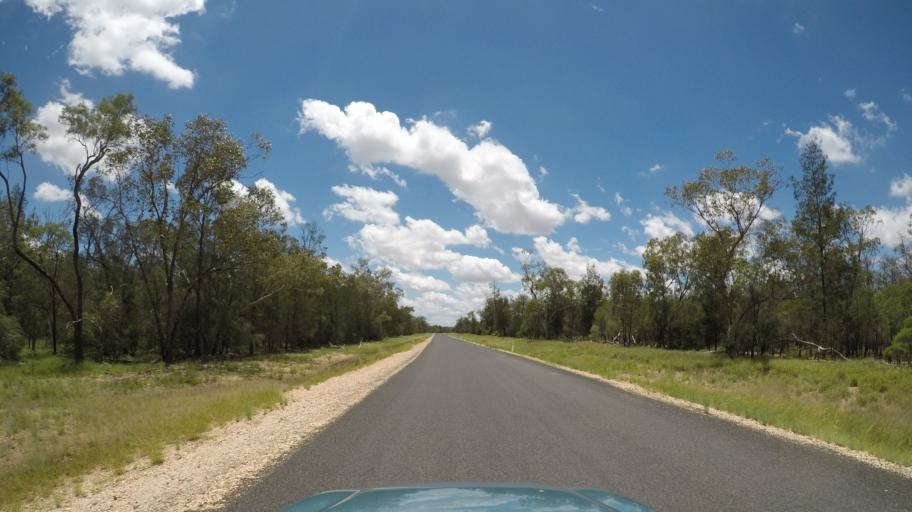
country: AU
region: Queensland
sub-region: Goondiwindi
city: Goondiwindi
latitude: -28.1545
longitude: 150.1231
